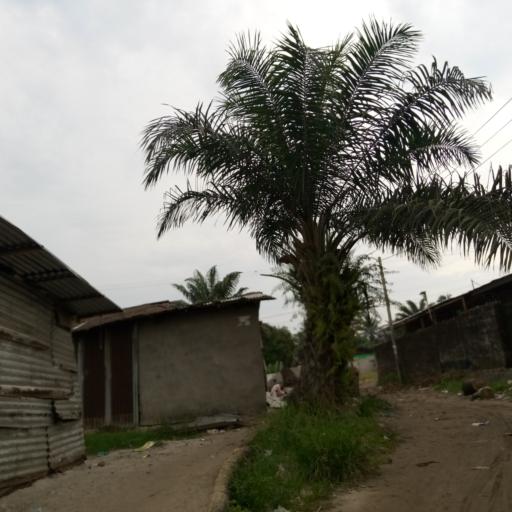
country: LR
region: Montserrado
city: Monrovia
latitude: 6.2936
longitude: -10.6838
